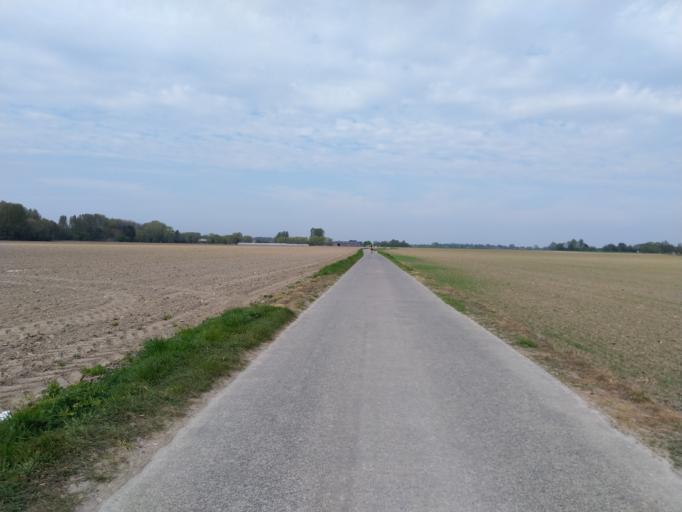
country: BE
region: Wallonia
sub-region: Province du Hainaut
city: Jurbise
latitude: 50.5125
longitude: 3.8808
